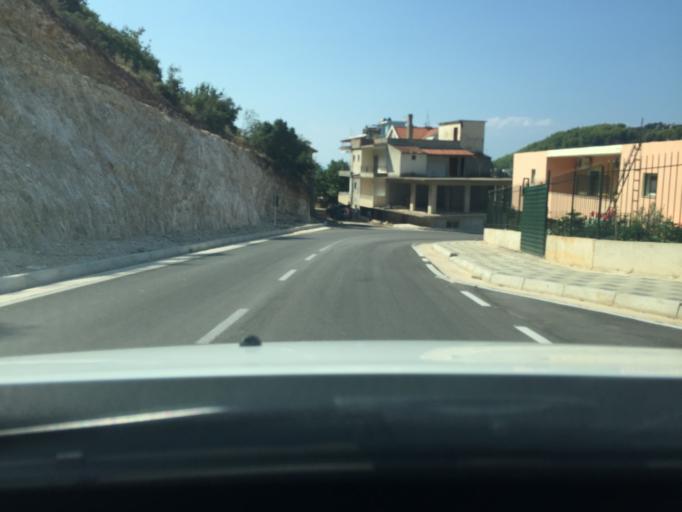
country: AL
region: Vlore
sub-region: Rrethi i Vlores
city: Himare
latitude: 40.1102
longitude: 19.7437
